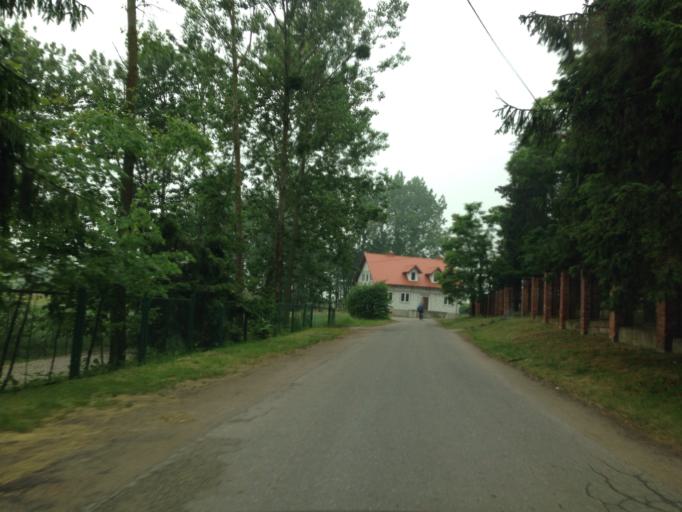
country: PL
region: Kujawsko-Pomorskie
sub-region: Powiat brodnicki
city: Jablonowo Pomorskie
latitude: 53.4270
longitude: 19.2015
